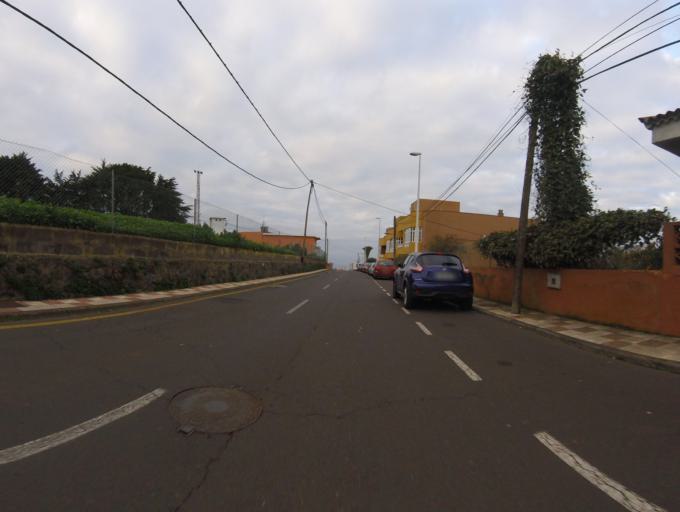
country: ES
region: Canary Islands
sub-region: Provincia de Santa Cruz de Tenerife
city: La Laguna
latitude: 28.4565
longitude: -16.3623
